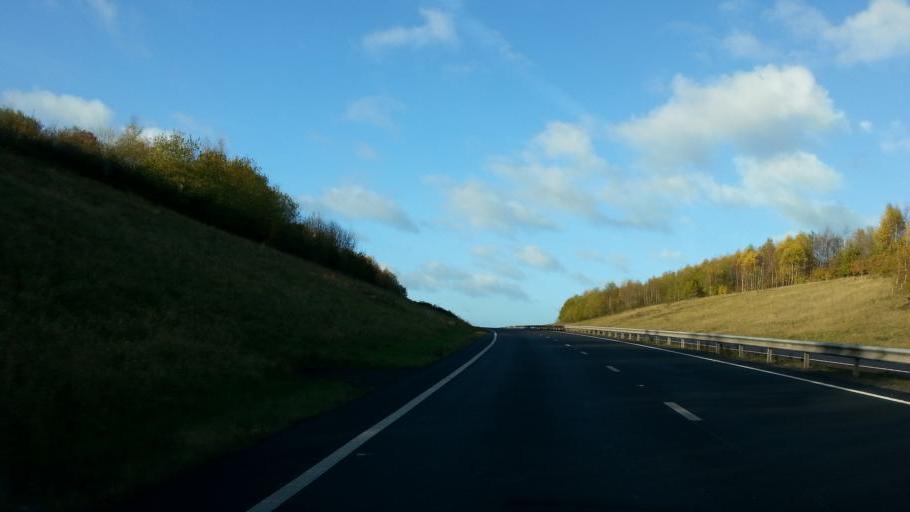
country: GB
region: England
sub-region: Staffordshire
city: Whittington
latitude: 52.6294
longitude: -1.7585
